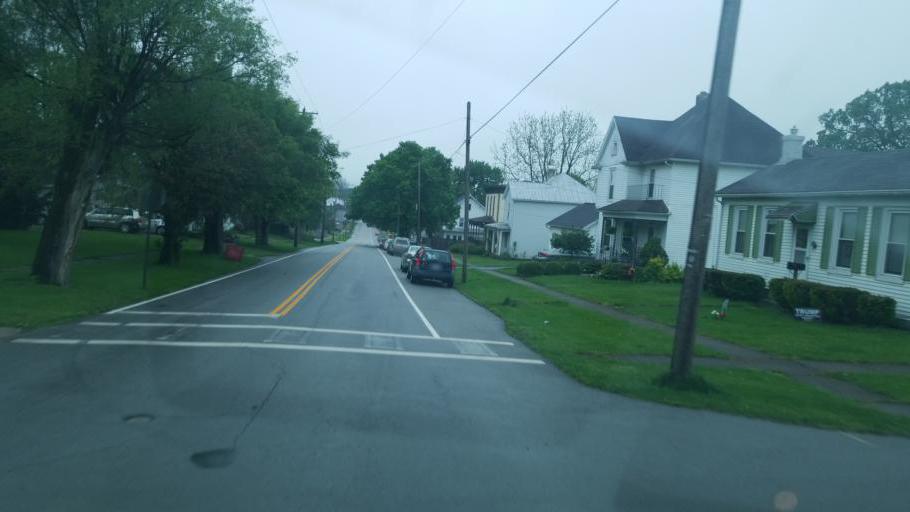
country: US
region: Ohio
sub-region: Highland County
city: Hillsboro
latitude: 39.2006
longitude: -83.6192
